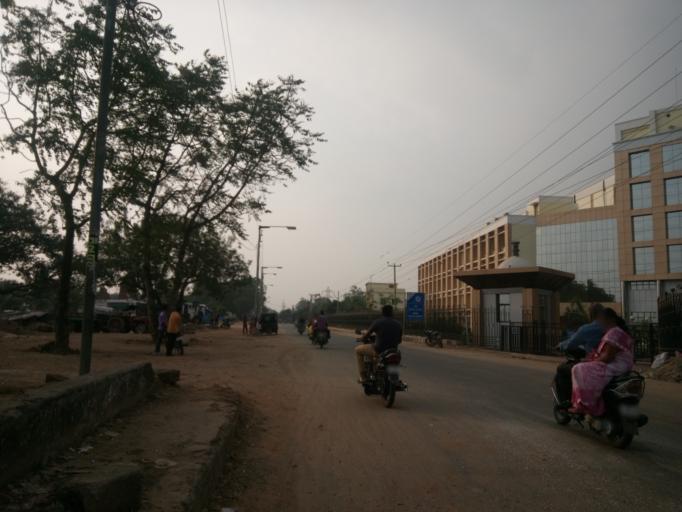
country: IN
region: Odisha
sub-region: Cuttack
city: Cuttack
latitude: 20.4673
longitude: 85.8545
